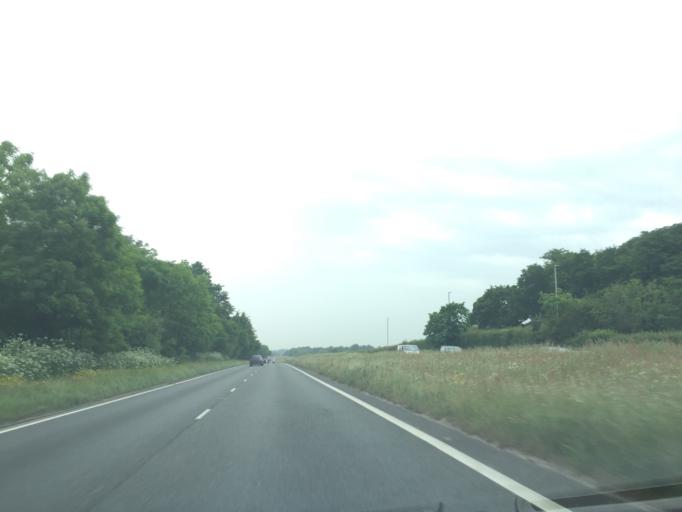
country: GB
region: England
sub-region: Poole
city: Poole
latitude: 50.7370
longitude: -2.0026
